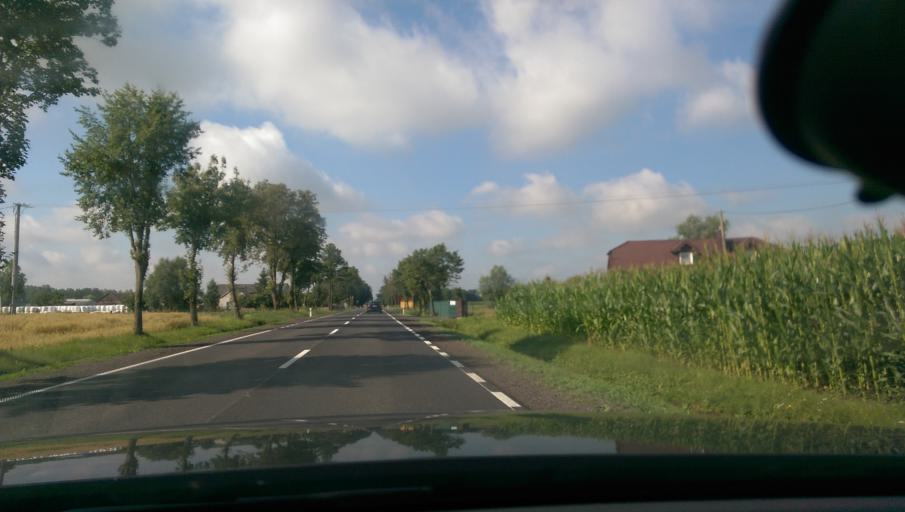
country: PL
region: Masovian Voivodeship
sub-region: Powiat ciechanowski
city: Ojrzen
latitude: 52.7346
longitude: 20.5179
